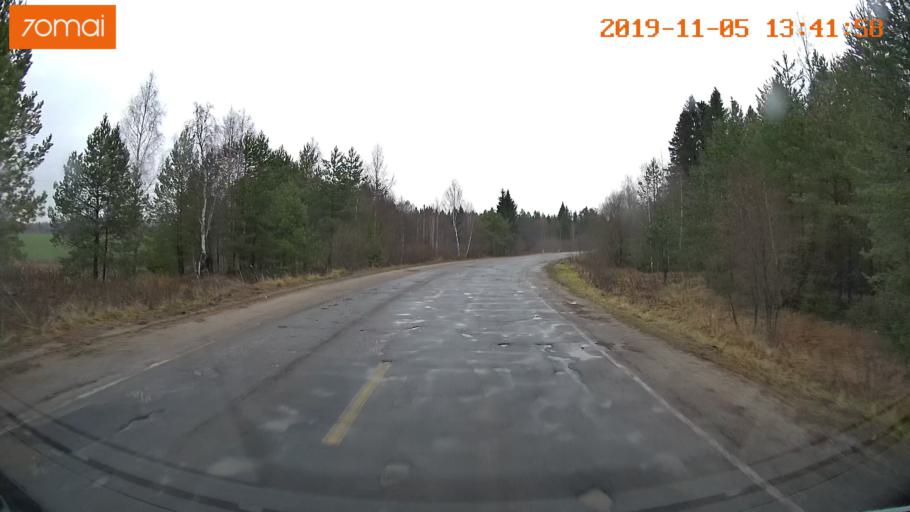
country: RU
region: Ivanovo
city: Shuya
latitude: 56.9635
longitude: 41.3888
